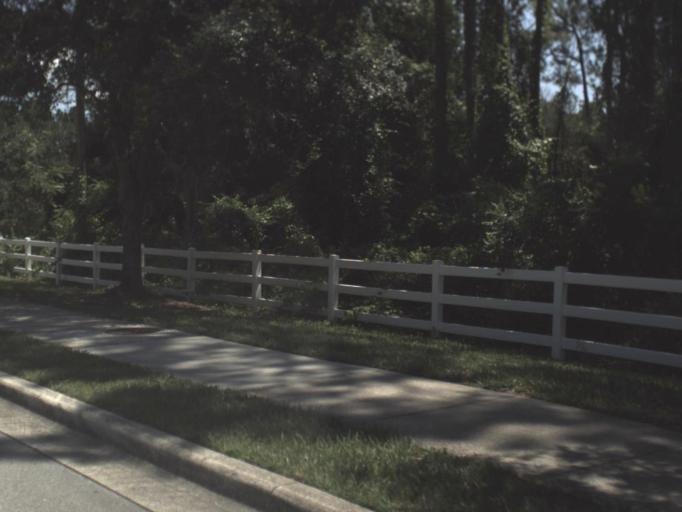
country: US
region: Florida
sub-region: Saint Johns County
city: Fruit Cove
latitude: 30.1103
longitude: -81.6263
